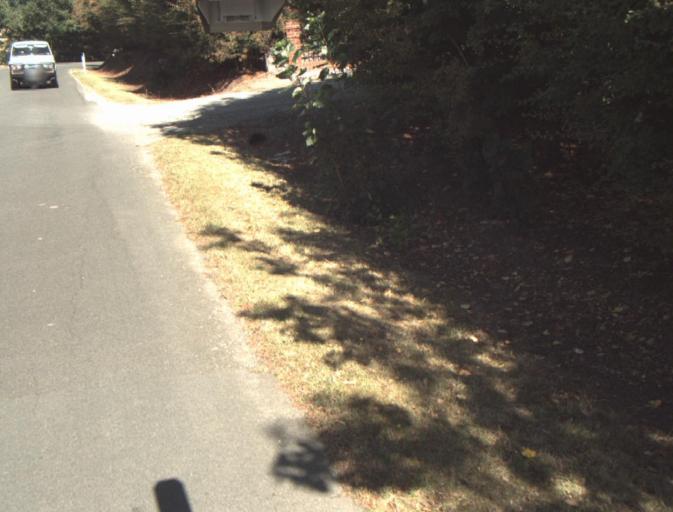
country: AU
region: Tasmania
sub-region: Launceston
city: Mayfield
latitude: -41.2411
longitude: 147.2318
